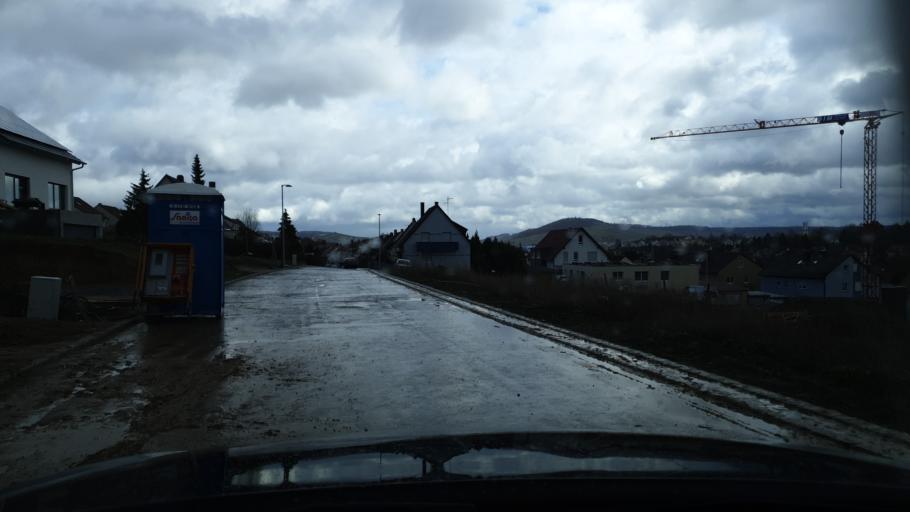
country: DE
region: Baden-Wuerttemberg
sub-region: Regierungsbezirk Stuttgart
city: Neckarsulm
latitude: 49.1686
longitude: 9.1877
